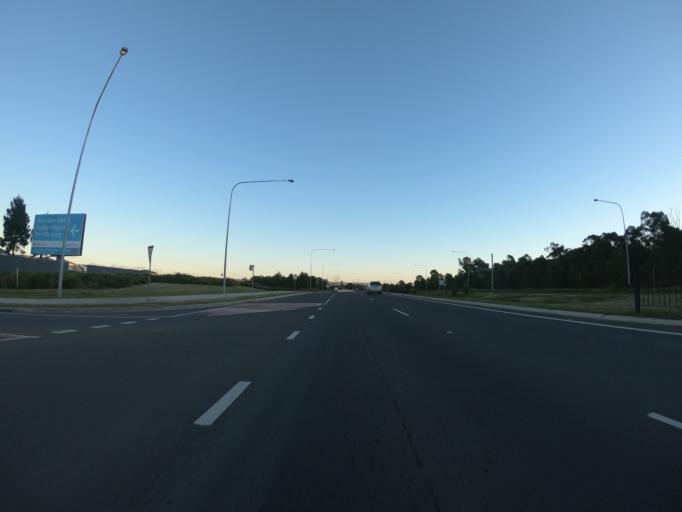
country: AU
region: New South Wales
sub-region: Blacktown
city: Riverstone
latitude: -33.6912
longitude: 150.8256
